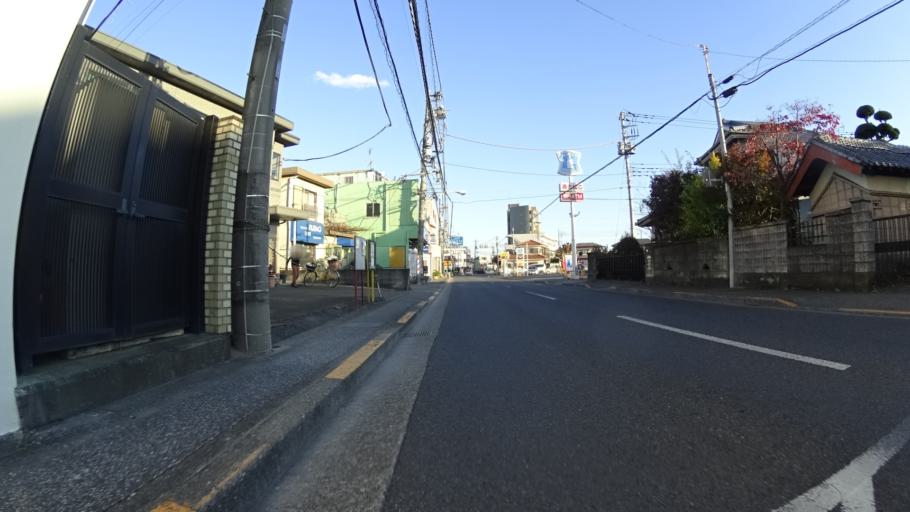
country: JP
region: Tokyo
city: Hachioji
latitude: 35.6738
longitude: 139.2942
